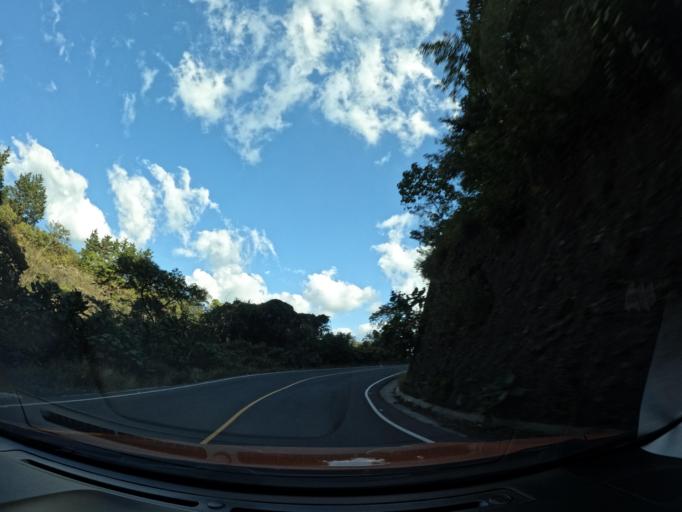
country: GT
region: Escuintla
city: Palin
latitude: 14.4584
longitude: -90.6961
